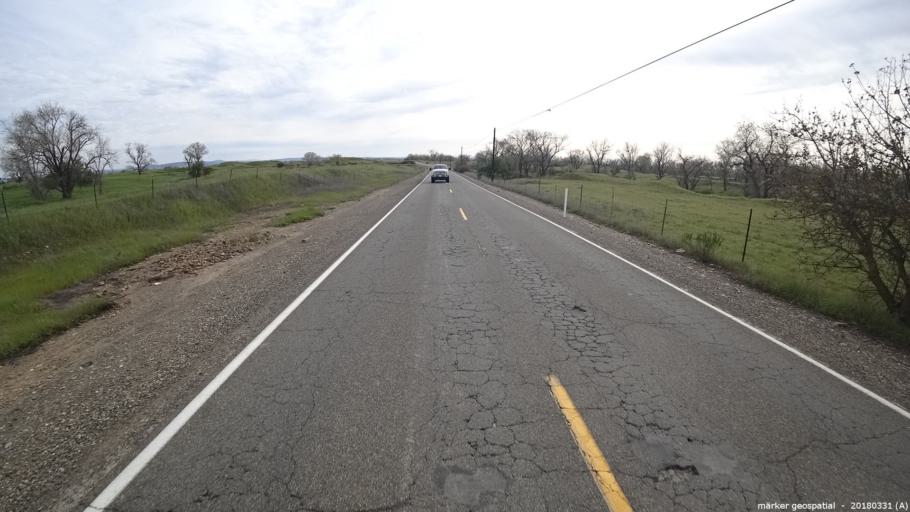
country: US
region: California
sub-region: Sacramento County
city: Gold River
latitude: 38.5939
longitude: -121.1925
